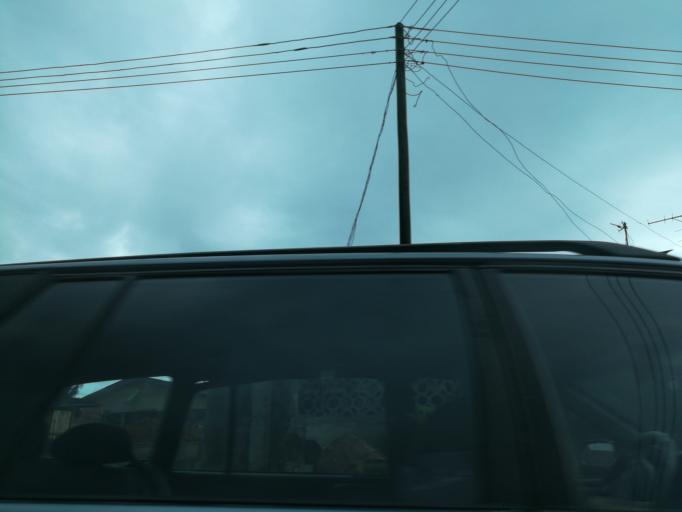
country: NG
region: Rivers
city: Port Harcourt
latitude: 4.8376
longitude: 7.0334
